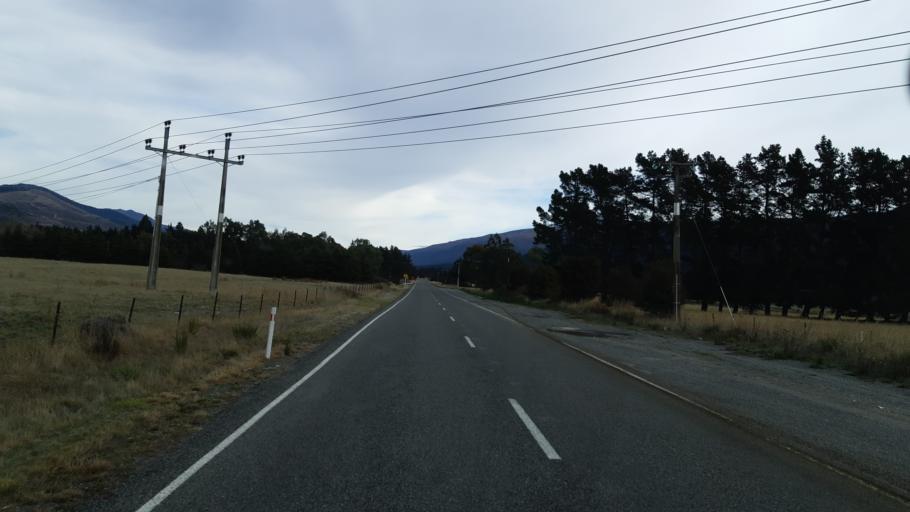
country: NZ
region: Tasman
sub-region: Tasman District
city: Brightwater
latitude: -41.6641
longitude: 173.2078
